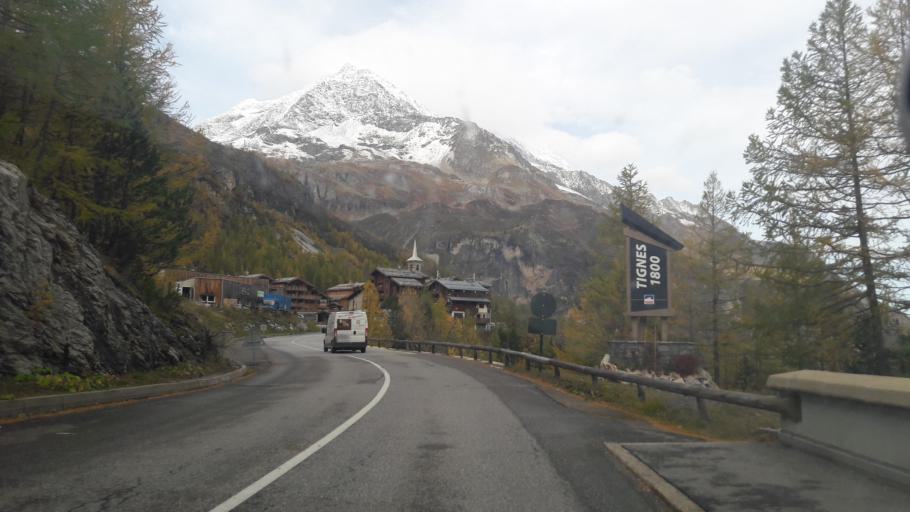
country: FR
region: Rhone-Alpes
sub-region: Departement de la Savoie
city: Tignes
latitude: 45.4952
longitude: 6.9298
